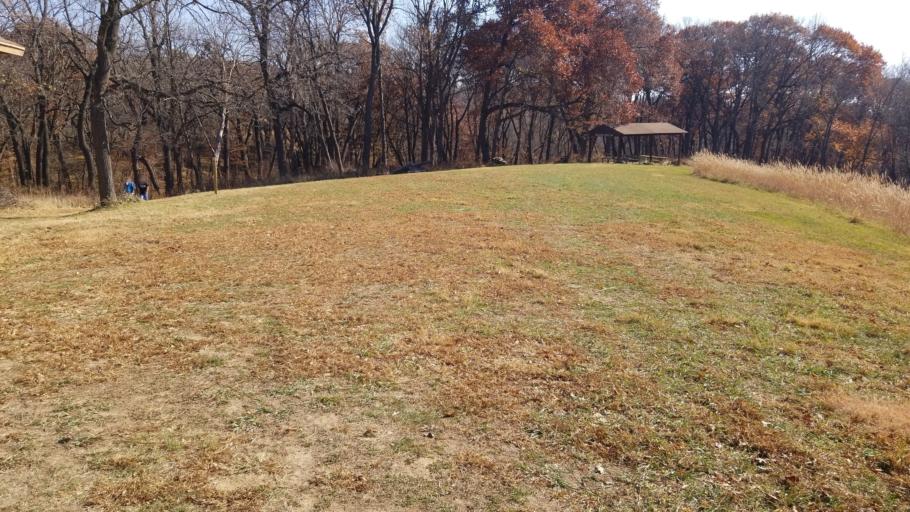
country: US
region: Nebraska
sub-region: Sarpy County
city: Bellevue
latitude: 41.1629
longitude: -95.8962
